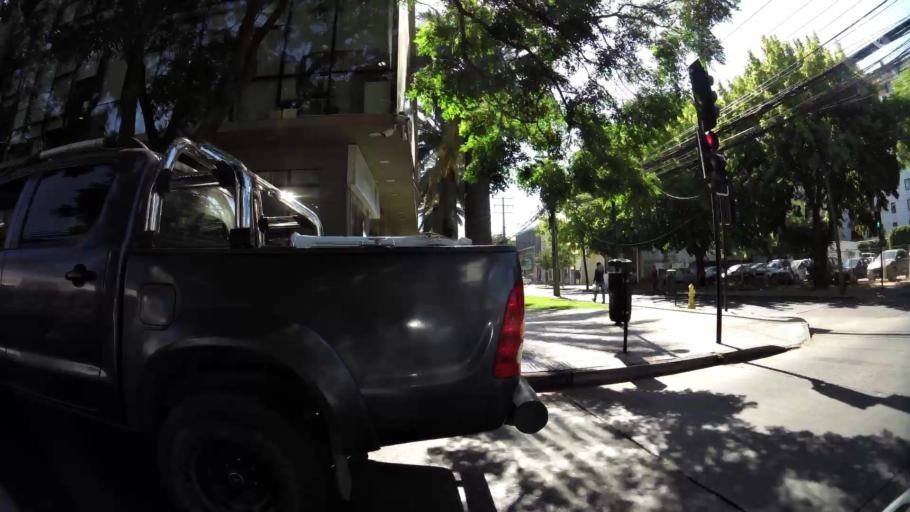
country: CL
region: Maule
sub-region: Provincia de Talca
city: Talca
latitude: -35.4248
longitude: -71.6652
